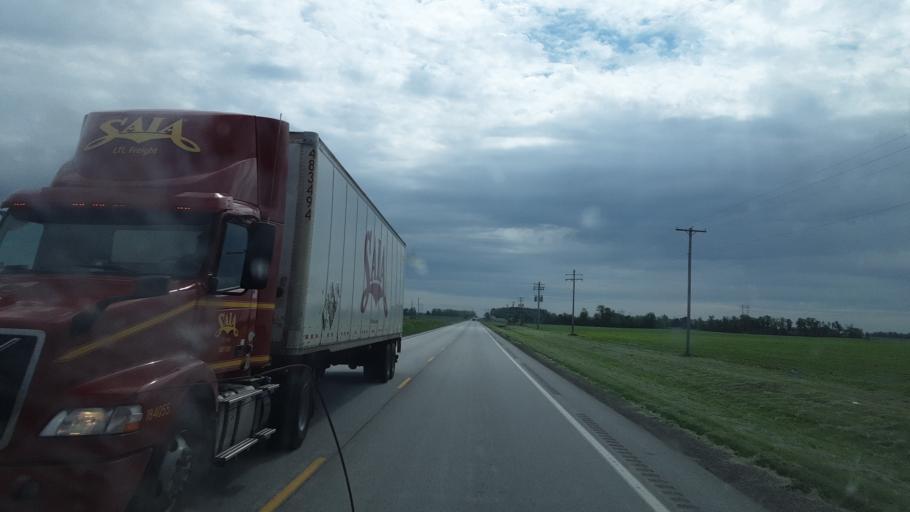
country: US
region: Illinois
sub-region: Mason County
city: Havana
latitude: 40.2975
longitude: -89.9591
